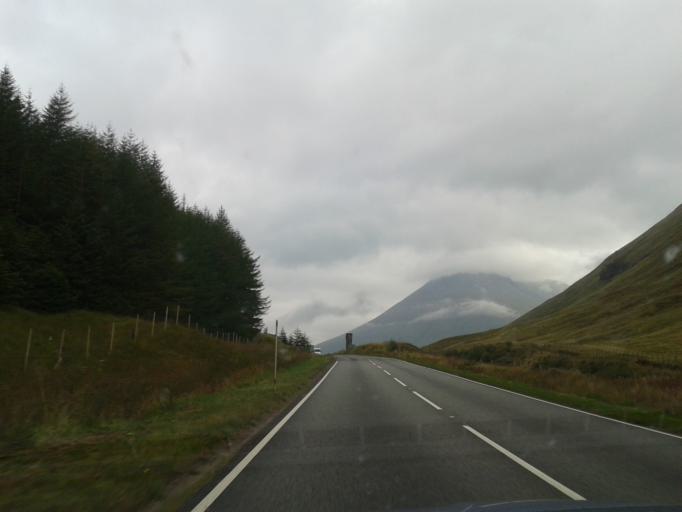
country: GB
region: Scotland
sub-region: Argyll and Bute
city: Garelochhead
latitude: 56.4581
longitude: -4.7130
